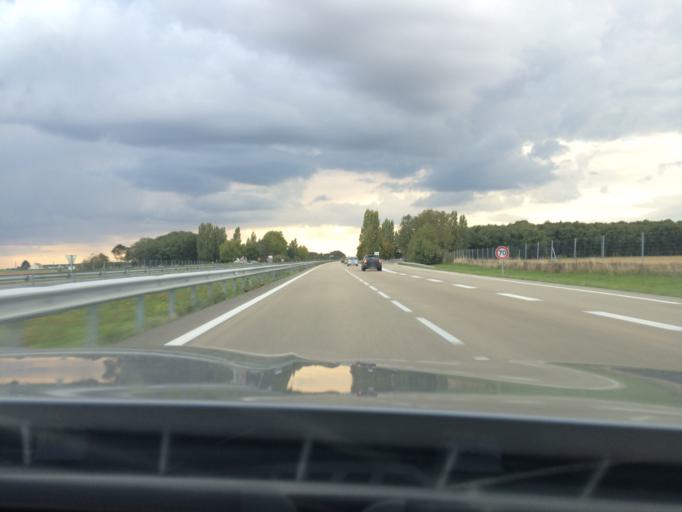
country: FR
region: Ile-de-France
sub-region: Departement de Seine-et-Marne
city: Egreville
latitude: 48.1847
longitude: 2.8308
